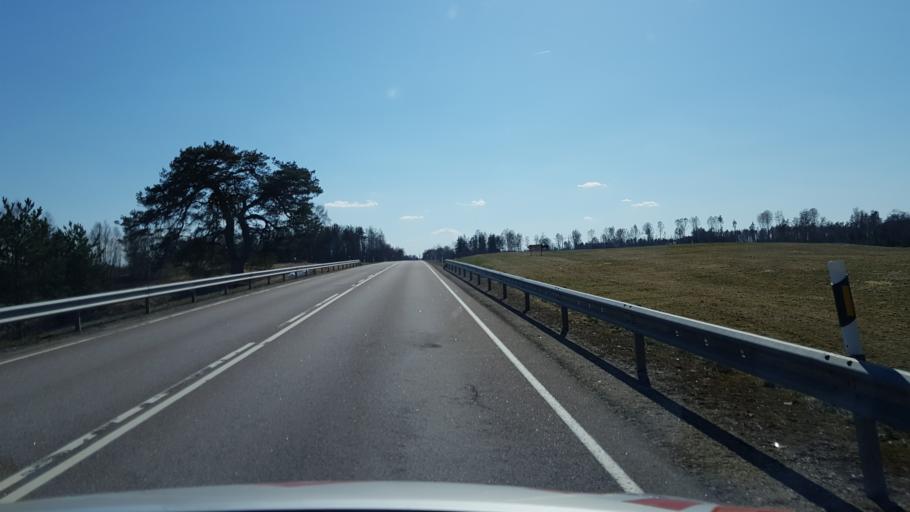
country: EE
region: Jogevamaa
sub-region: Mustvee linn
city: Mustvee
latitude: 58.7197
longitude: 26.8291
